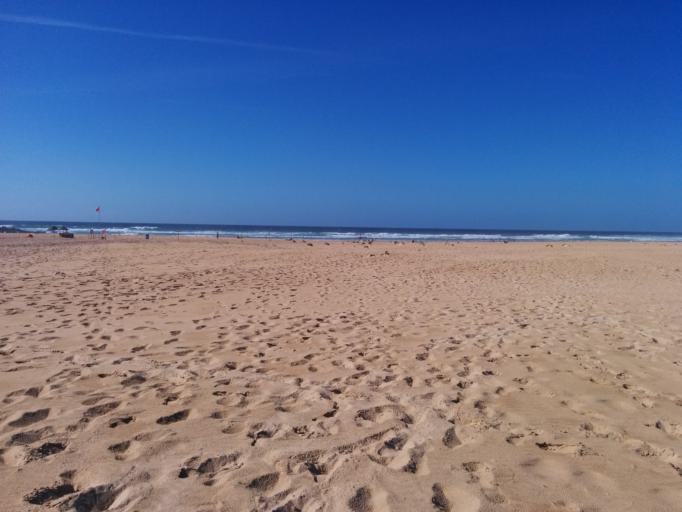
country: PT
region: Faro
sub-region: Vila do Bispo
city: Vila do Bispo
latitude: 37.1973
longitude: -8.9023
